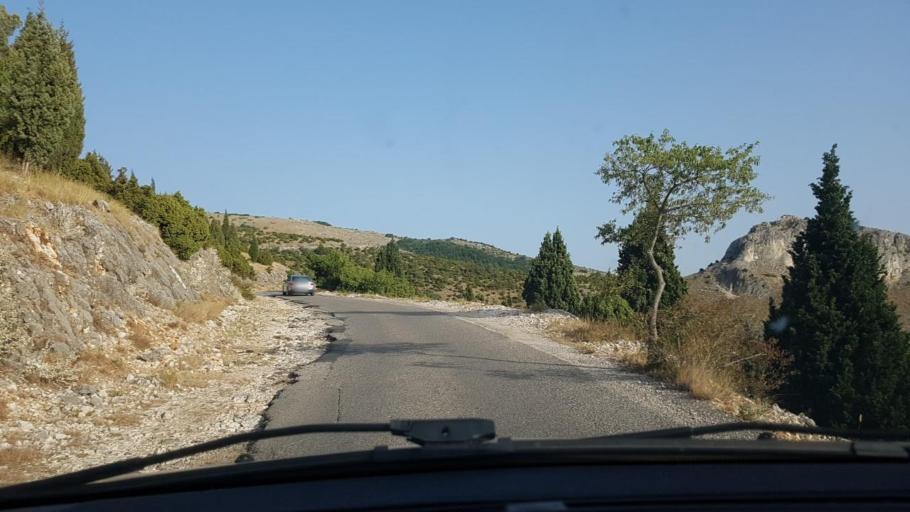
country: BA
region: Federation of Bosnia and Herzegovina
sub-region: Hercegovacko-Bosanski Kanton
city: Mostar
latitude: 43.3489
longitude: 17.8279
